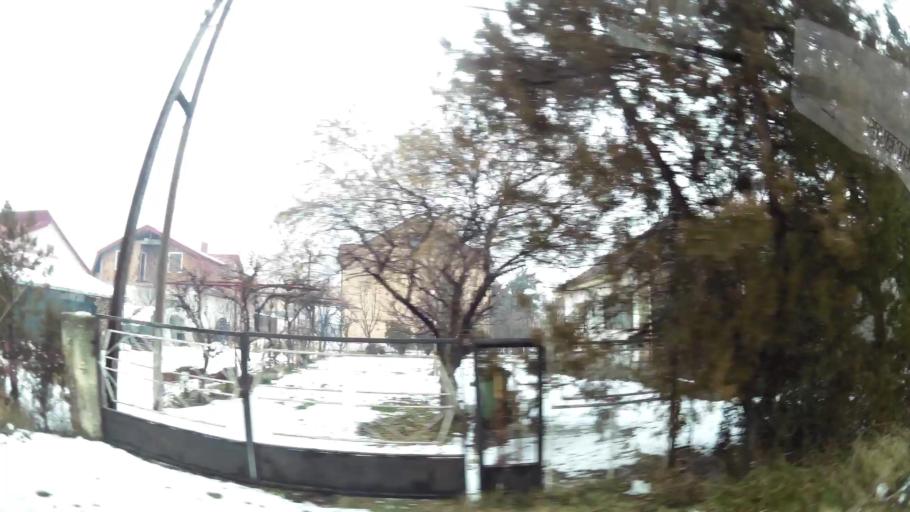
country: MK
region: Petrovec
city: Petrovec
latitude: 41.9401
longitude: 21.6147
